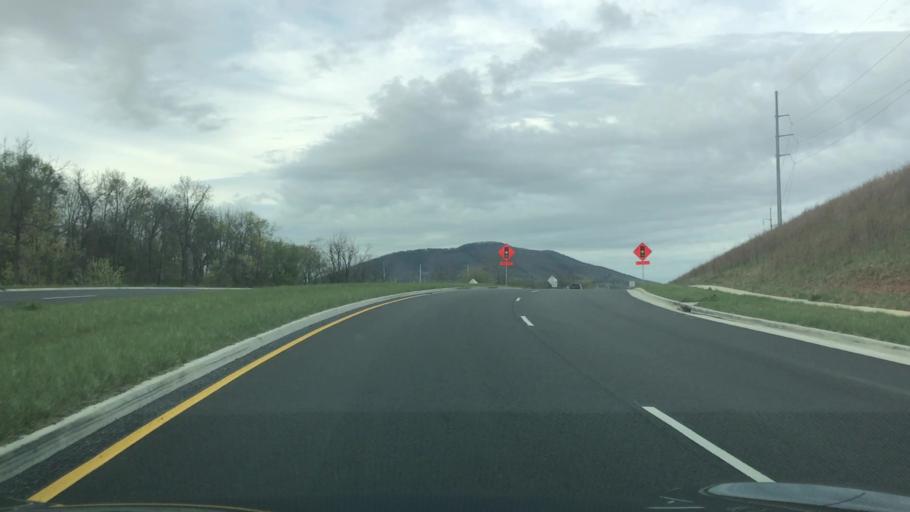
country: US
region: Virginia
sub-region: Botetourt County
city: Cloverdale
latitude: 37.3878
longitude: -79.8964
